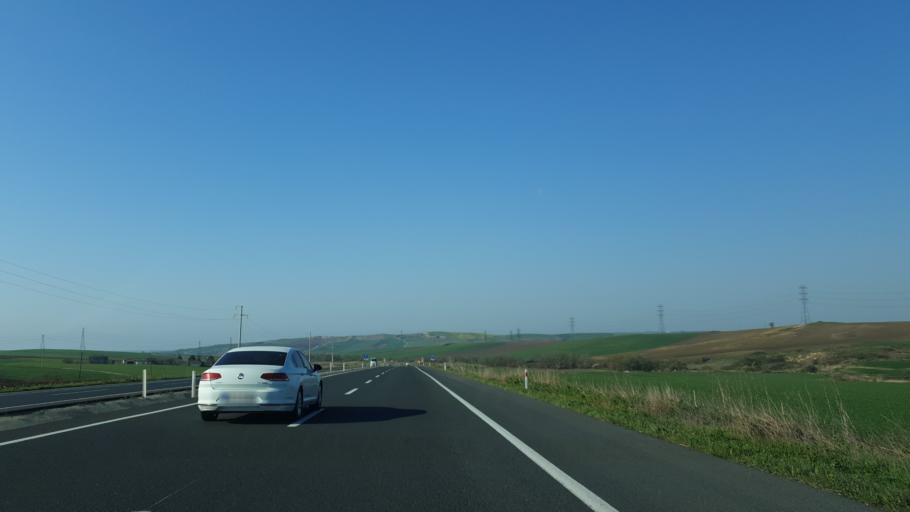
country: TR
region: Tekirdag
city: Corlu
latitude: 41.0897
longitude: 27.7460
